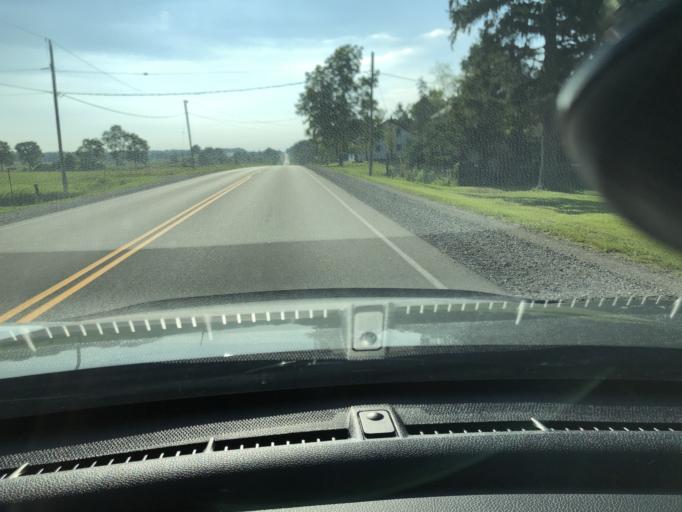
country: CA
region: Ontario
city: Stratford
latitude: 43.4243
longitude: -80.7857
